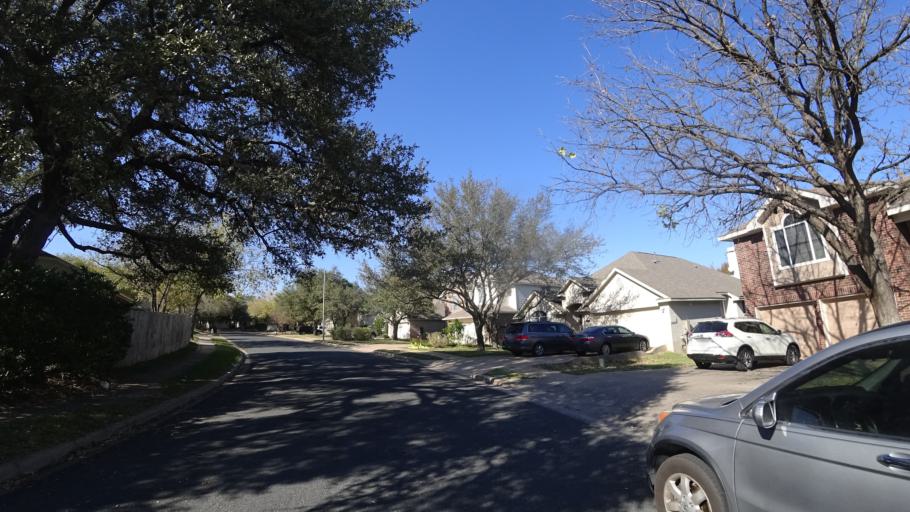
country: US
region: Texas
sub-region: Travis County
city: Barton Creek
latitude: 30.2277
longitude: -97.8652
